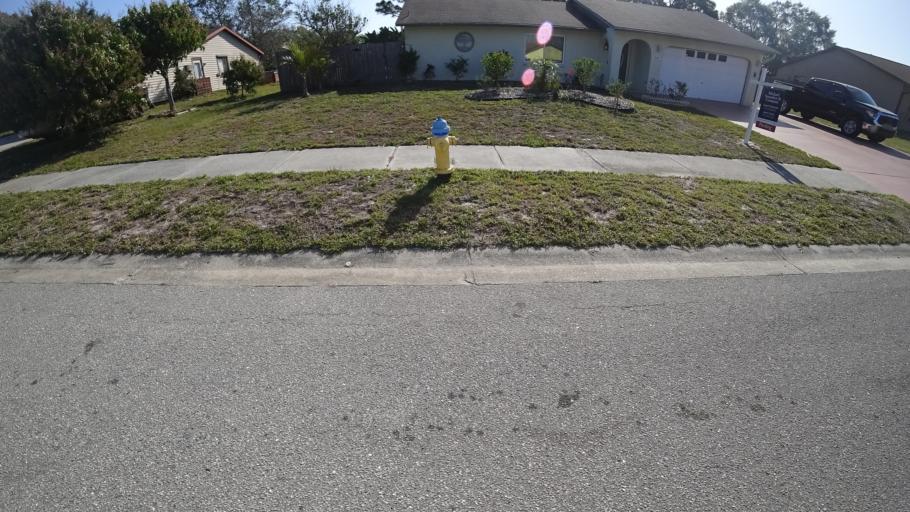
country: US
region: Florida
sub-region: Manatee County
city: Whitfield
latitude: 27.4104
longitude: -82.5596
